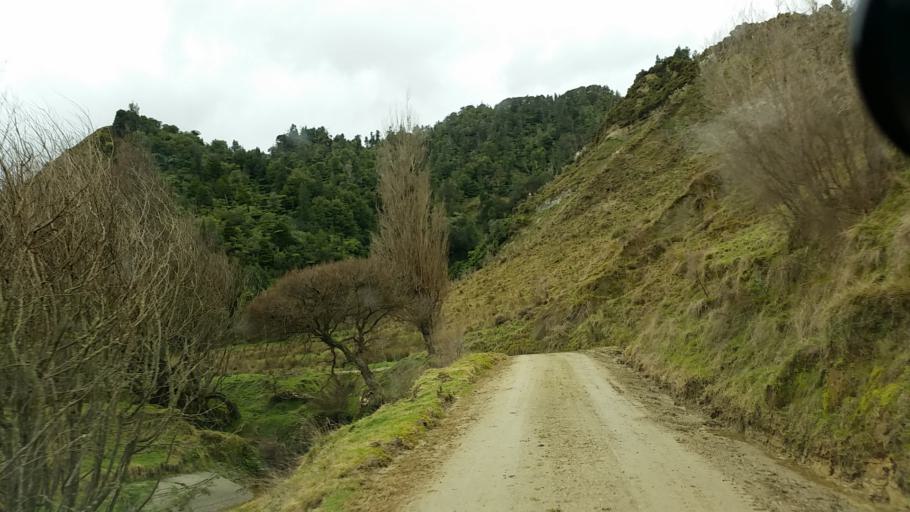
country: NZ
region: Taranaki
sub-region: South Taranaki District
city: Patea
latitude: -39.6589
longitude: 174.7510
